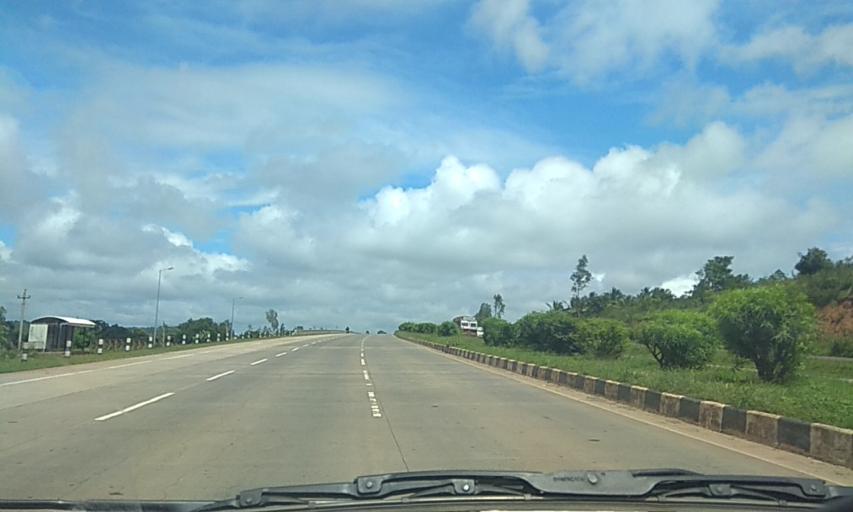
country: IN
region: Karnataka
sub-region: Dharwad
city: Alnavar
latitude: 15.6135
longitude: 74.7641
